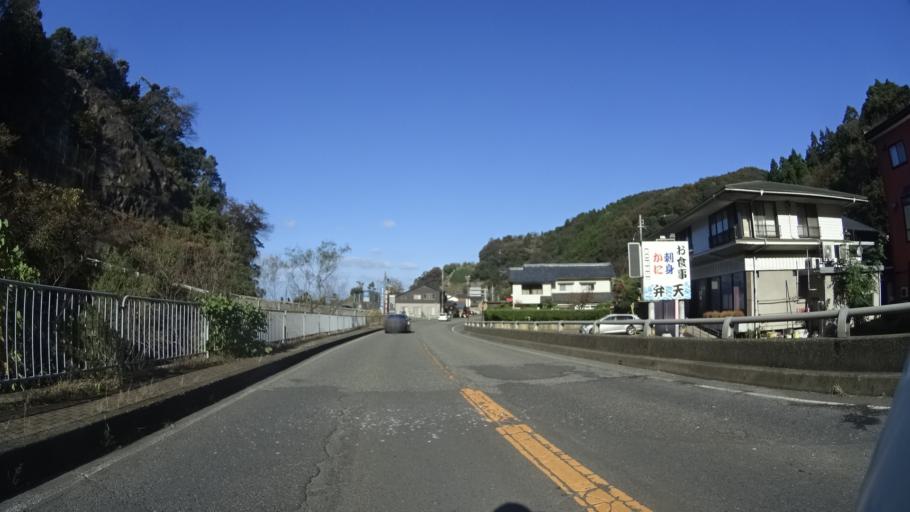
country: JP
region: Fukui
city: Takefu
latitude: 35.8215
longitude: 136.0735
